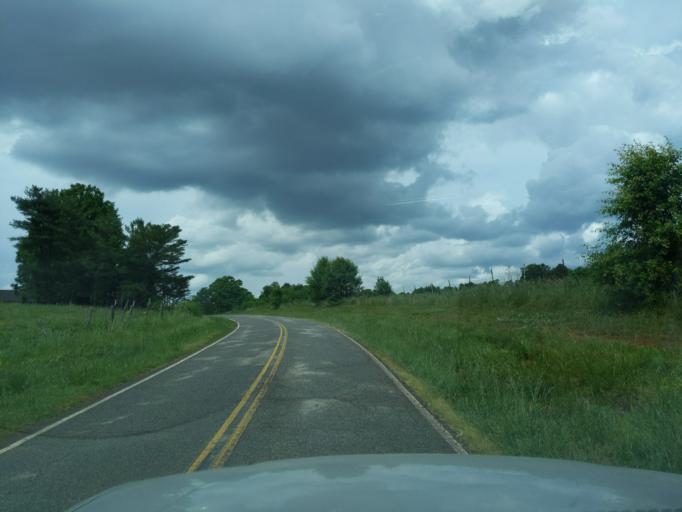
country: US
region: South Carolina
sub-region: Spartanburg County
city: Inman Mills
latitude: 35.0086
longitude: -82.1180
